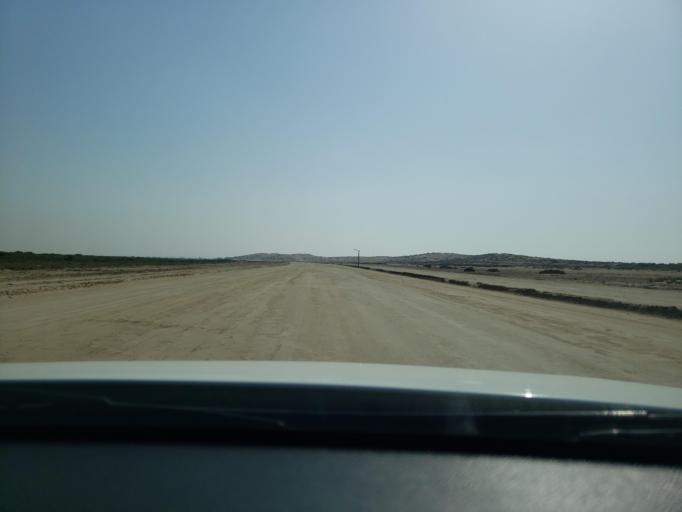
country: AE
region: Umm al Qaywayn
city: Umm al Qaywayn
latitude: 25.5347
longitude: 55.6155
